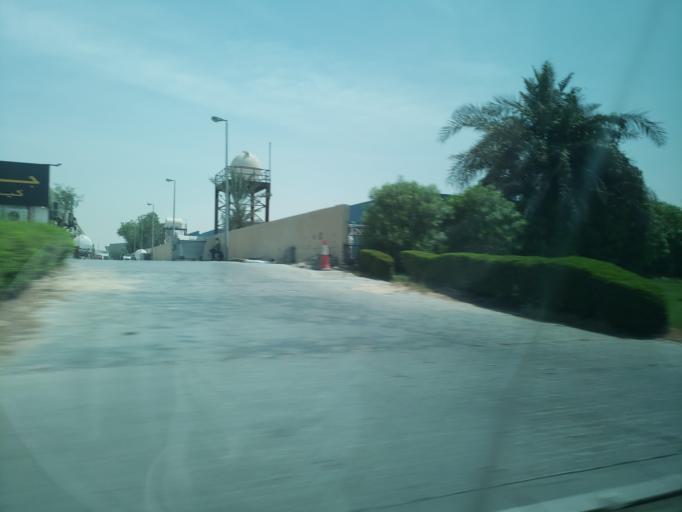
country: AE
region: Ash Shariqah
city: Sharjah
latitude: 25.3312
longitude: 55.4936
